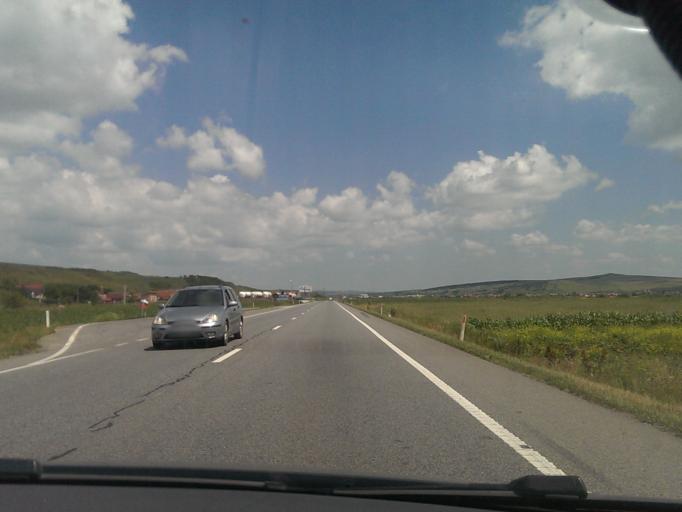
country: RO
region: Cluj
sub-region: Comuna Apahida
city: Sannicoara
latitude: 46.8002
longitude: 23.7233
